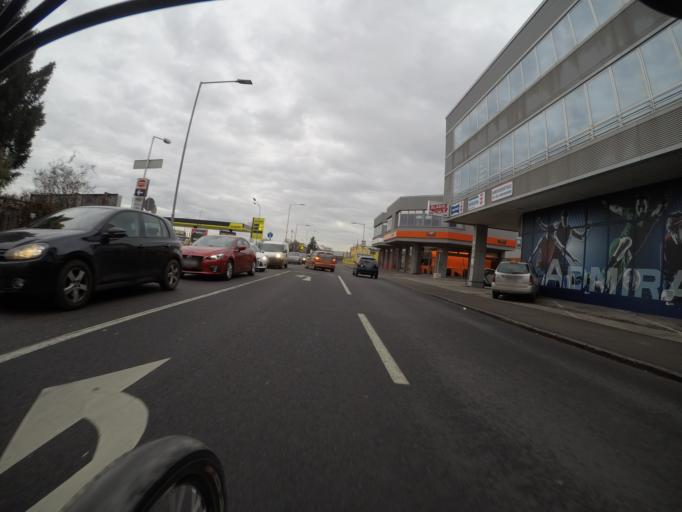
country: AT
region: Lower Austria
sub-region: Politischer Bezirk Modling
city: Vosendorf
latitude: 48.1249
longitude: 16.3215
